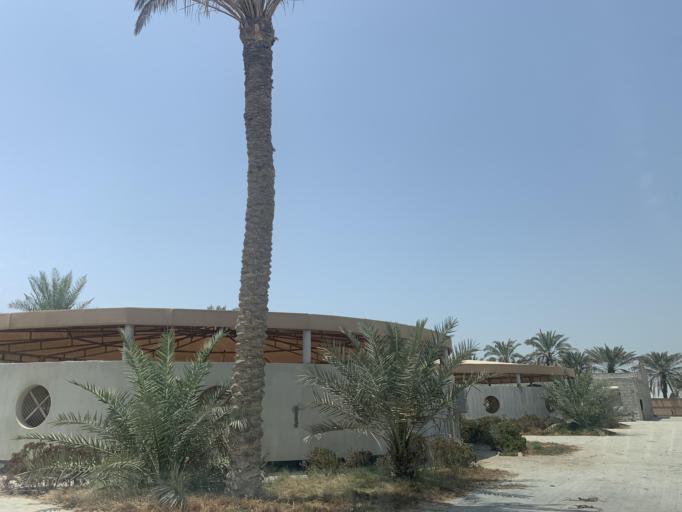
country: BH
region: Central Governorate
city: Madinat Hamad
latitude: 26.1621
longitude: 50.4916
